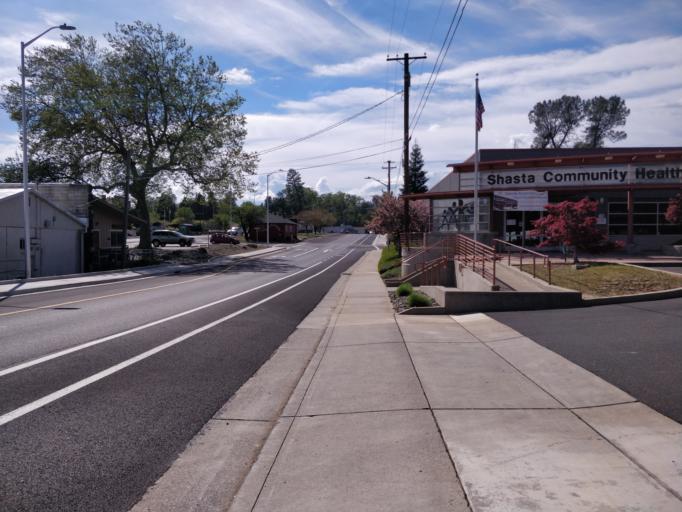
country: US
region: California
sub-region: Shasta County
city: Shasta Lake
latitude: 40.6811
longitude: -122.3698
